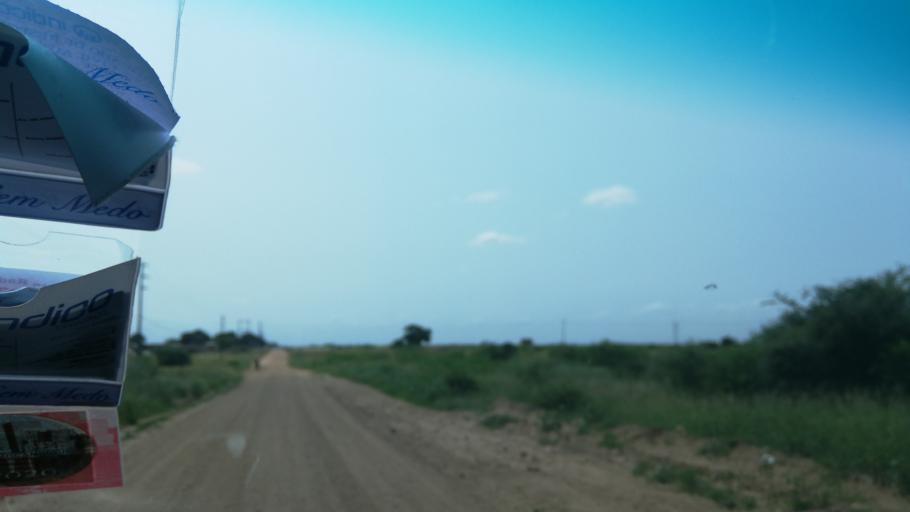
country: MZ
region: Maputo
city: Matola
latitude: -26.0681
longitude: 32.3905
